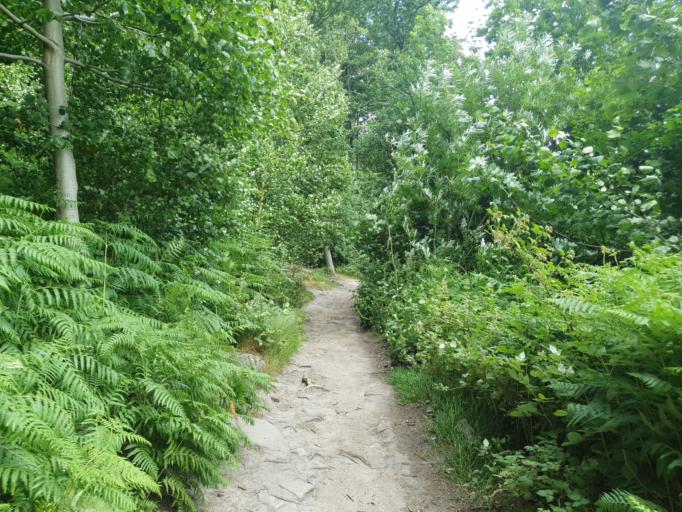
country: GB
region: England
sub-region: City and Borough of Leeds
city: Guiseley
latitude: 53.8598
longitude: -1.7166
